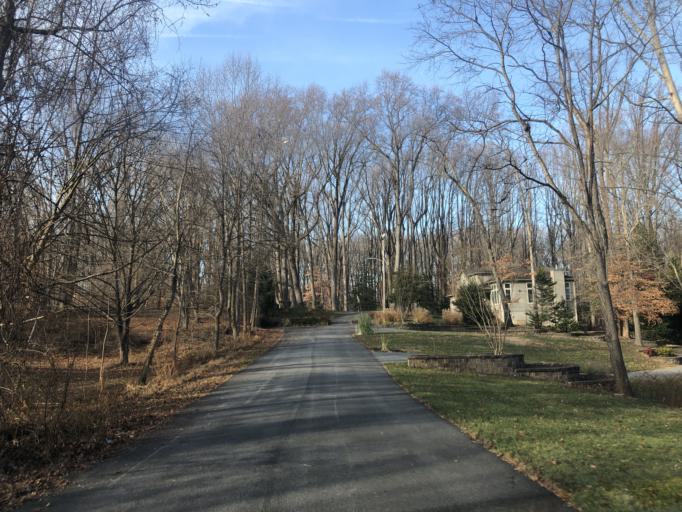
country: US
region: Maryland
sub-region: Anne Arundel County
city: Crownsville
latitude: 39.0414
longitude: -76.6036
